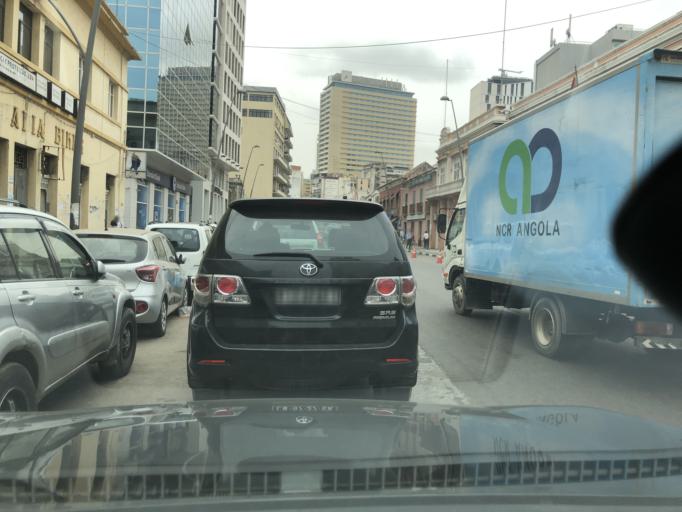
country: AO
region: Luanda
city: Luanda
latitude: -8.8135
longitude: 13.2317
